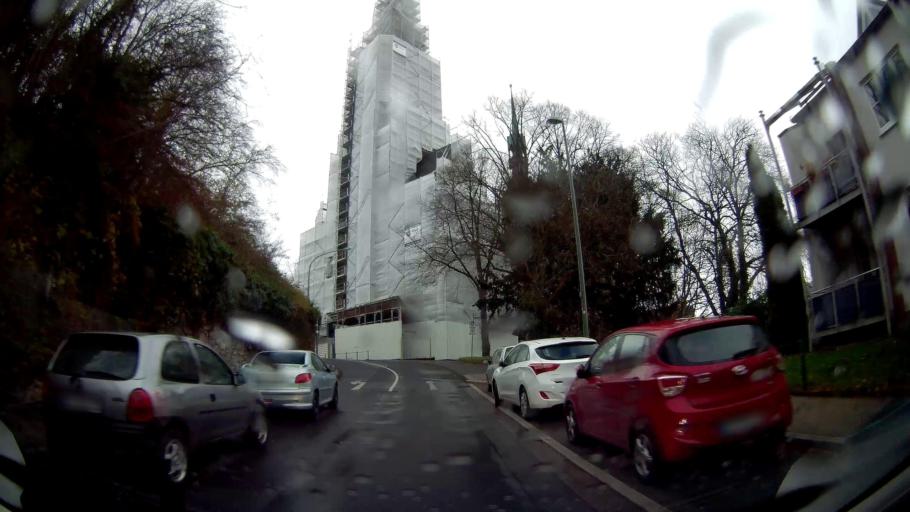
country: DE
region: North Rhine-Westphalia
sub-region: Regierungsbezirk Dusseldorf
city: Essen
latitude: 51.4475
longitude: 7.0739
